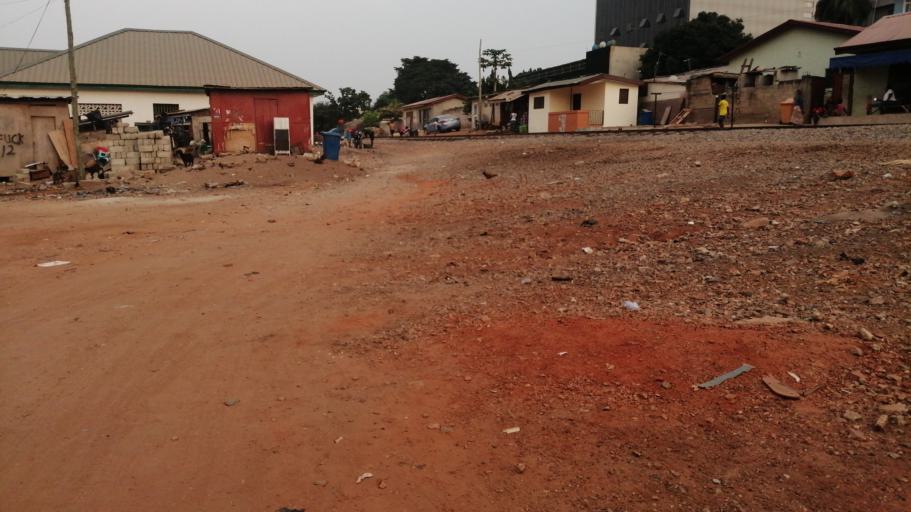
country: GH
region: Greater Accra
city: Medina Estates
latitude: 5.6185
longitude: -0.1791
